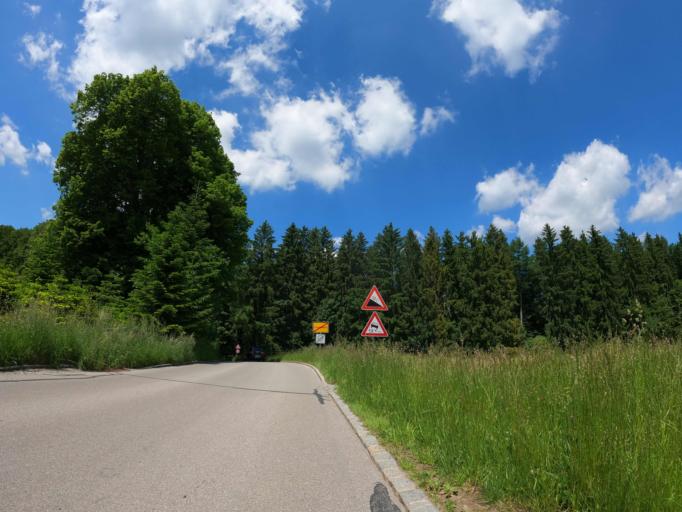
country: DE
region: Bavaria
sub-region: Upper Bavaria
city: Strasslach-Dingharting
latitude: 47.9926
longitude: 11.5599
